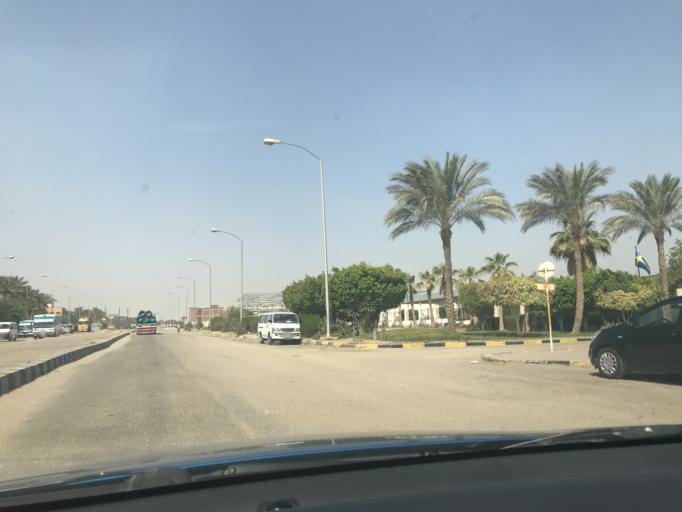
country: EG
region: Eastern Province
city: Bilbays
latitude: 30.2471
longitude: 31.7592
